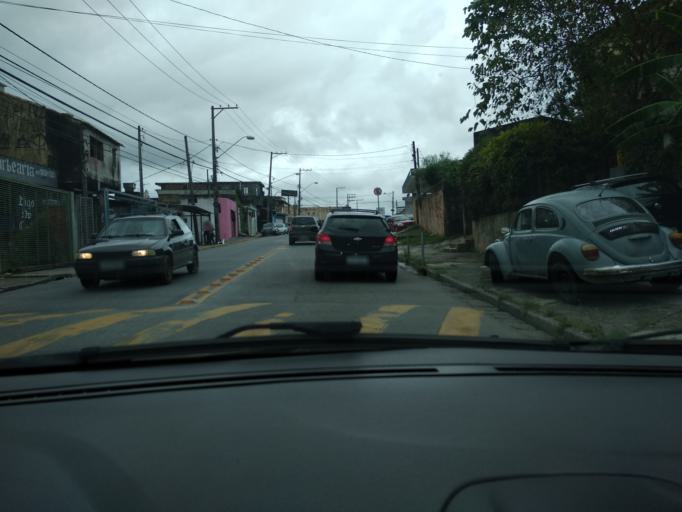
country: BR
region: Sao Paulo
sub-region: Mogi das Cruzes
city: Mogi das Cruzes
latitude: -23.5356
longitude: -46.1937
